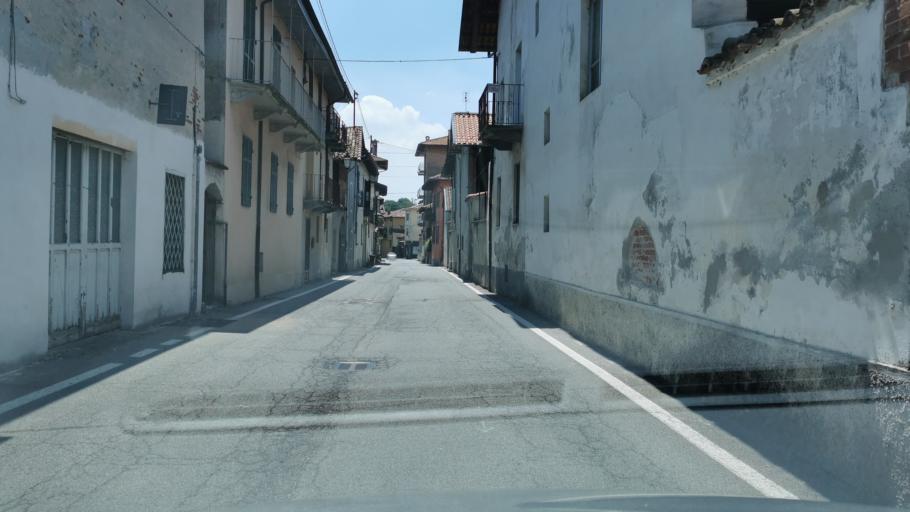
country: IT
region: Piedmont
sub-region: Provincia di Torino
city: Aglie
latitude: 45.3666
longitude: 7.7685
